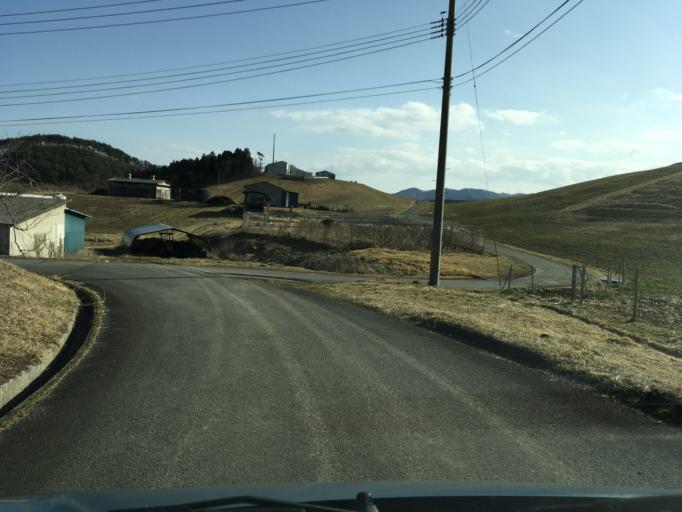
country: JP
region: Iwate
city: Ichinoseki
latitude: 38.7982
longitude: 141.4455
